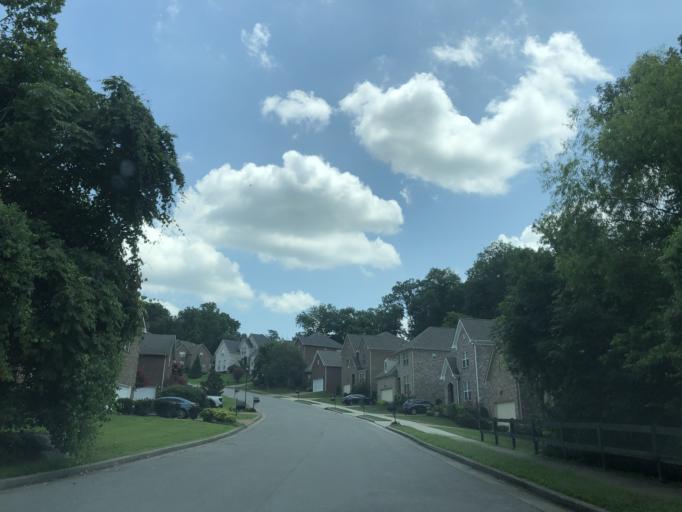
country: US
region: Tennessee
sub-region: Williamson County
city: Brentwood Estates
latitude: 36.0178
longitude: -86.7168
